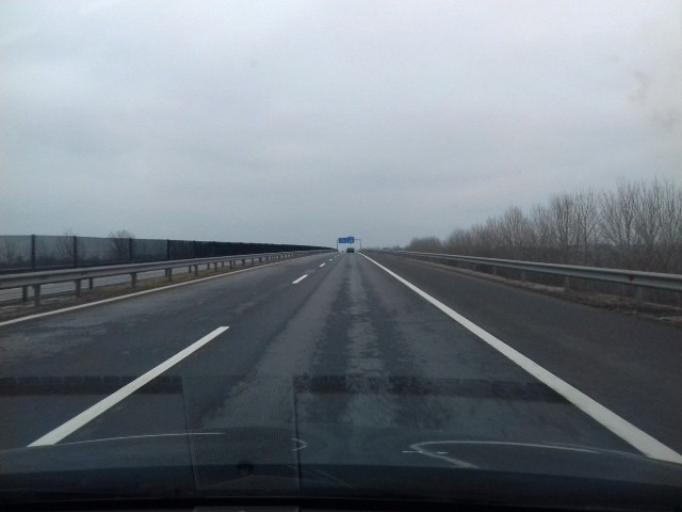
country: HU
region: Szabolcs-Szatmar-Bereg
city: Nagykallo
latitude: 47.8889
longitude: 21.7724
